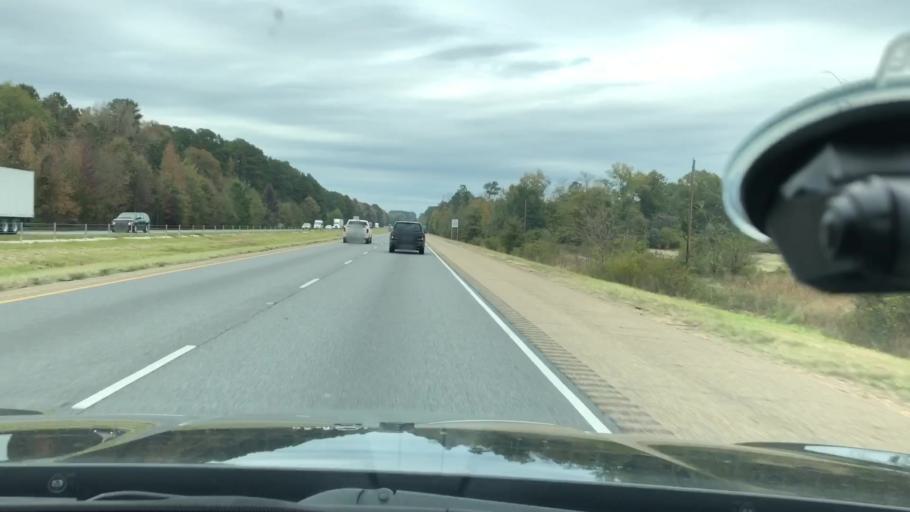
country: US
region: Arkansas
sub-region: Clark County
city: Gurdon
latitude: 33.9076
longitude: -93.2909
